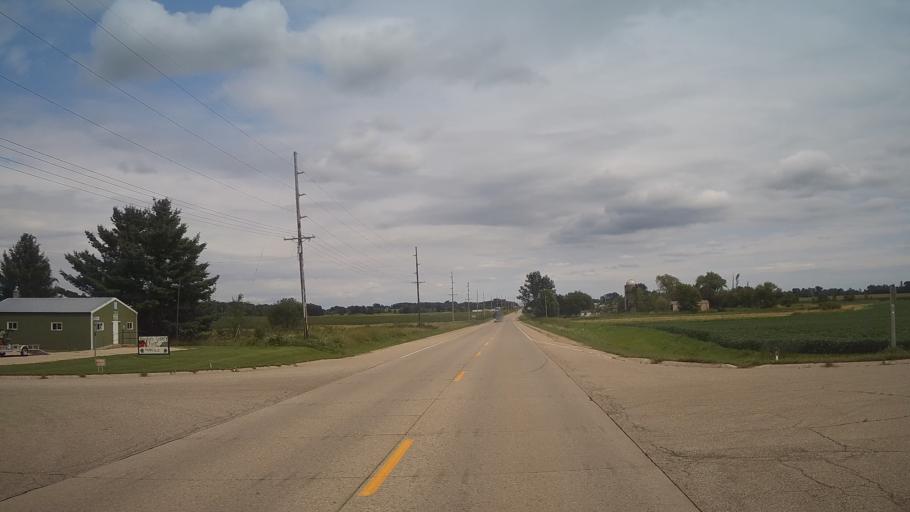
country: US
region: Wisconsin
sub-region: Waushara County
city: Redgranite
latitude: 44.0413
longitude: -89.0319
